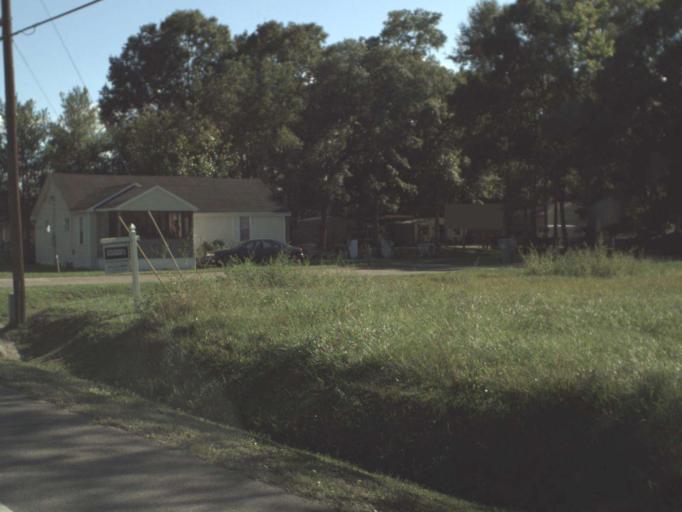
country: US
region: Florida
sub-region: Gulf County
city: Wewahitchka
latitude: 30.0986
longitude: -85.1996
